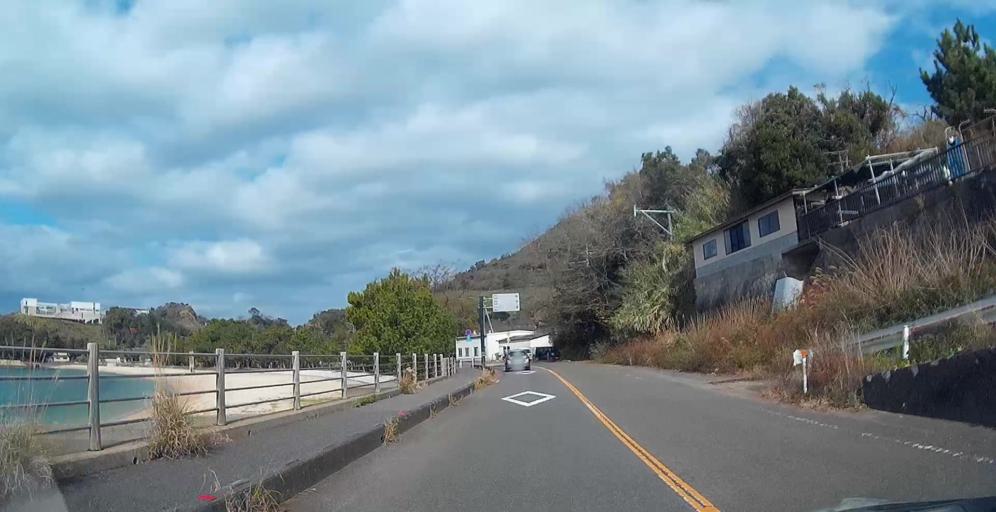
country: JP
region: Kumamoto
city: Minamata
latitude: 32.3162
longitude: 130.4718
